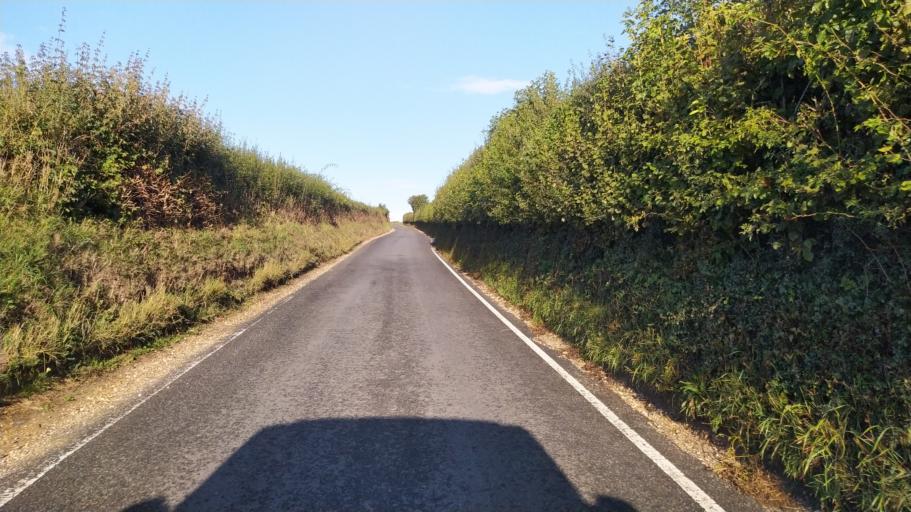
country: GB
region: England
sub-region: Dorset
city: Wimborne Minster
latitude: 50.8827
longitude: -1.9869
